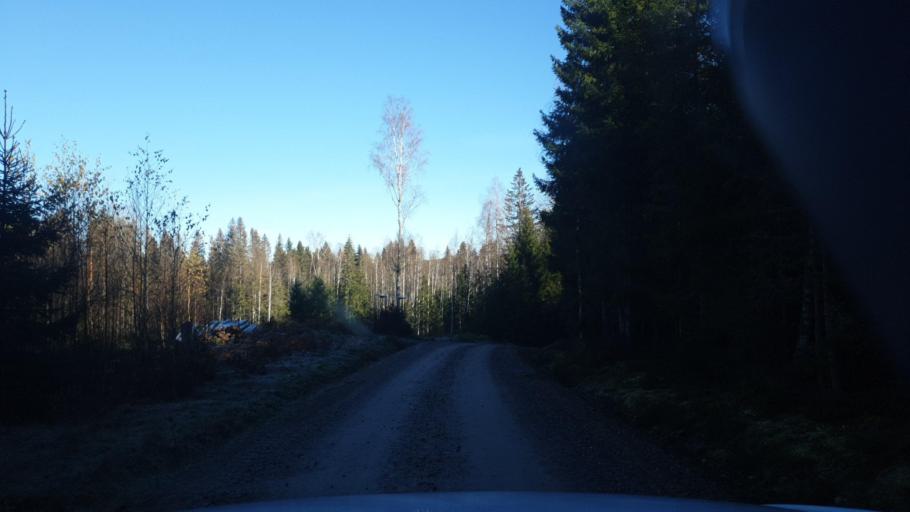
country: SE
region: Vaermland
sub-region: Karlstads Kommun
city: Edsvalla
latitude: 59.4819
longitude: 13.1434
